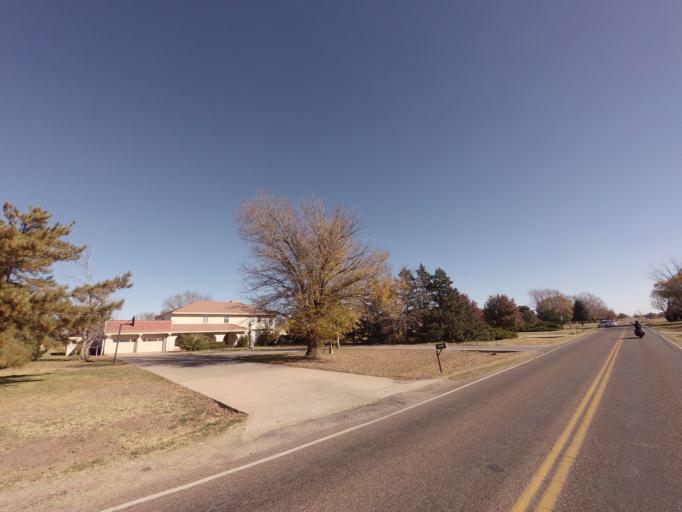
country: US
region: New Mexico
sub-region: Curry County
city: Clovis
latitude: 34.4193
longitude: -103.1753
